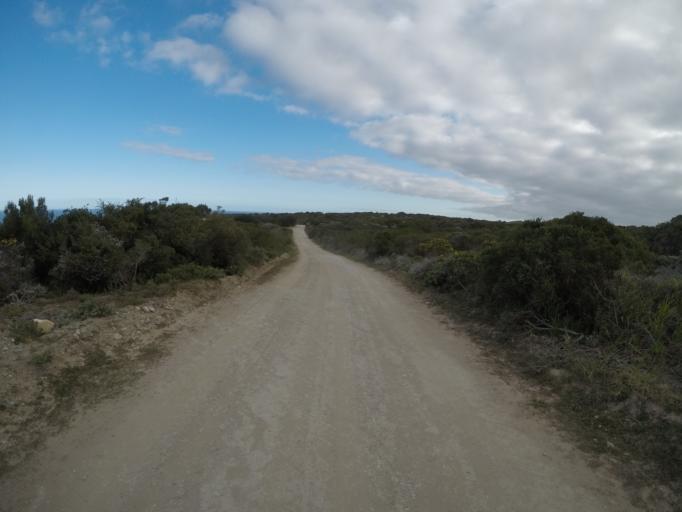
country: ZA
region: Western Cape
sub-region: Eden District Municipality
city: Riversdale
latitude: -34.4222
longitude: 21.3309
